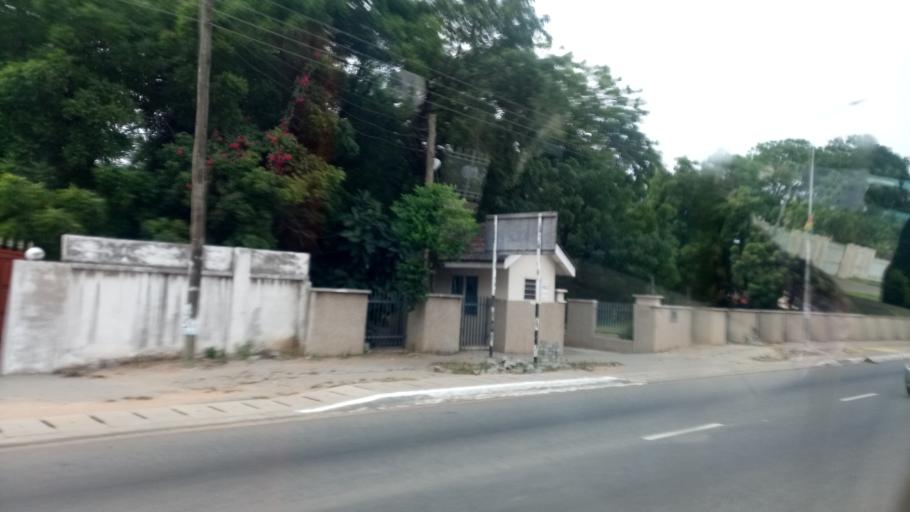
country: GH
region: Greater Accra
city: Accra
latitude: 5.5674
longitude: -0.1930
